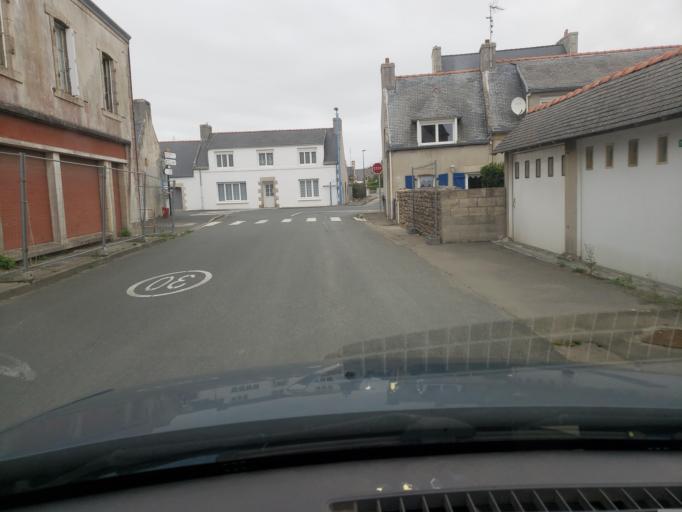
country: FR
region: Brittany
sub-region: Departement du Finistere
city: Guilvinec
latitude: 47.8012
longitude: -4.3577
